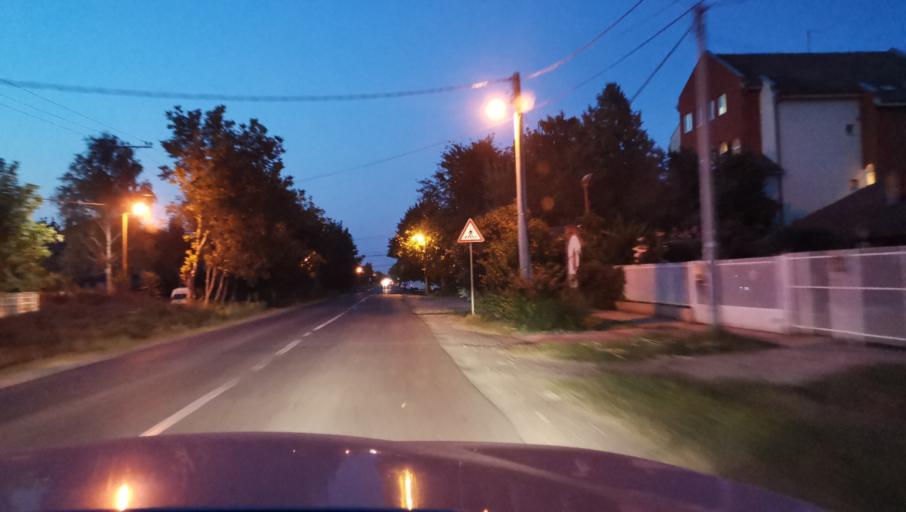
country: RS
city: Boljevci
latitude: 44.7436
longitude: 20.2529
